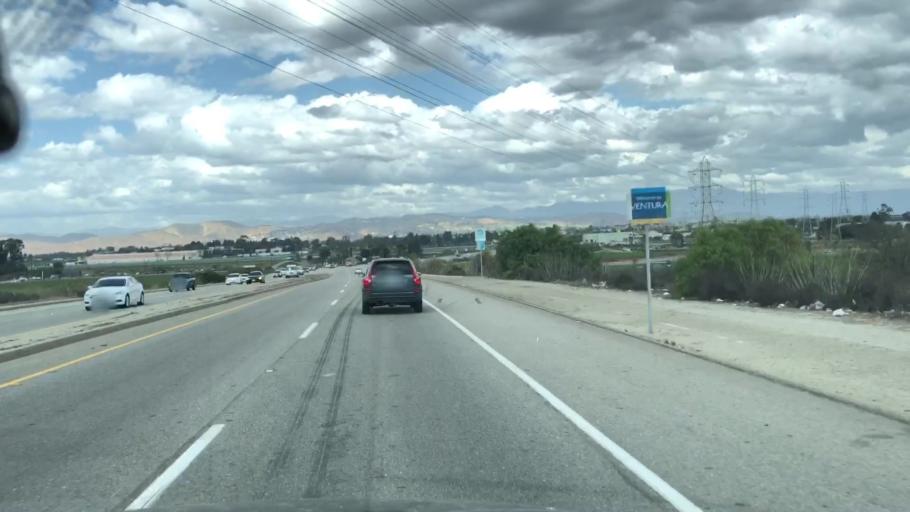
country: US
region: California
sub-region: Ventura County
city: El Rio
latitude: 34.2374
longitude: -119.2164
